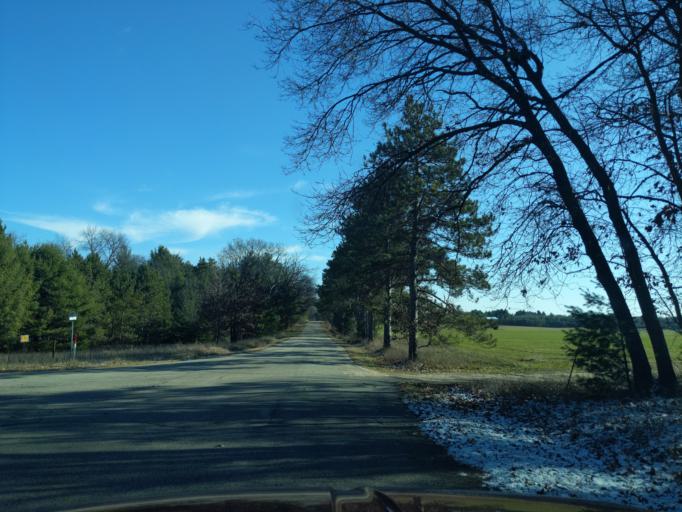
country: US
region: Wisconsin
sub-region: Waushara County
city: Silver Lake
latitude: 44.1052
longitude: -89.1691
